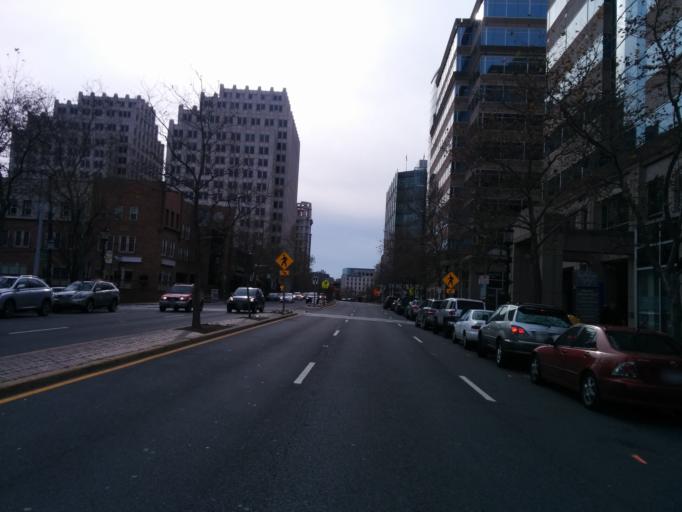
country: US
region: Maryland
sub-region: Montgomery County
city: Bethesda
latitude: 38.9872
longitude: -77.0949
